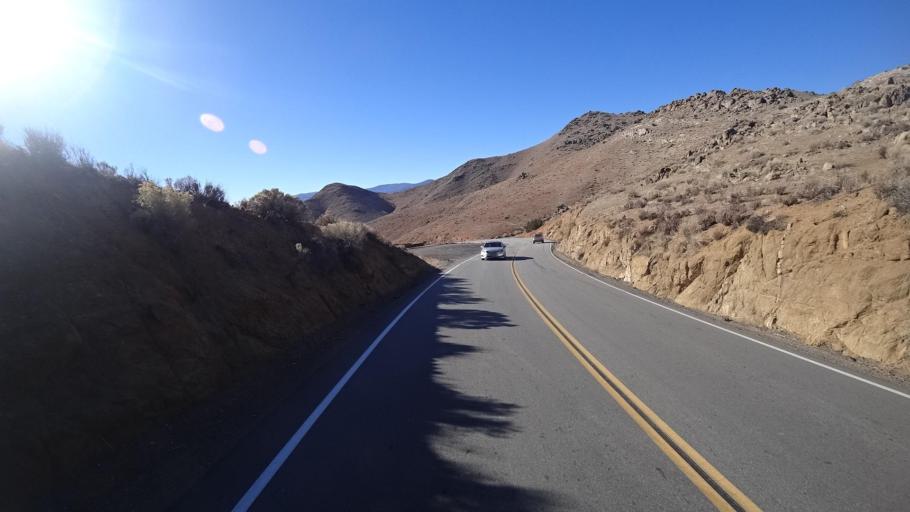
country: US
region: California
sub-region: Kern County
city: Wofford Heights
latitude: 35.6824
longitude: -118.3889
